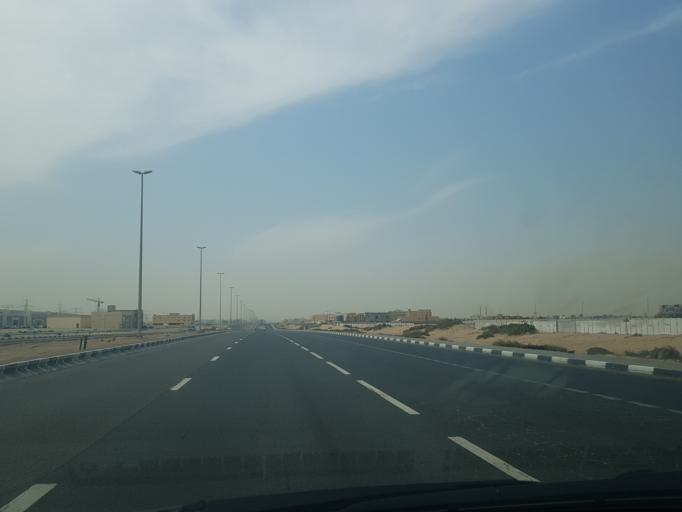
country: AE
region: Ash Shariqah
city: Sharjah
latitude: 25.2602
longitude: 55.5091
